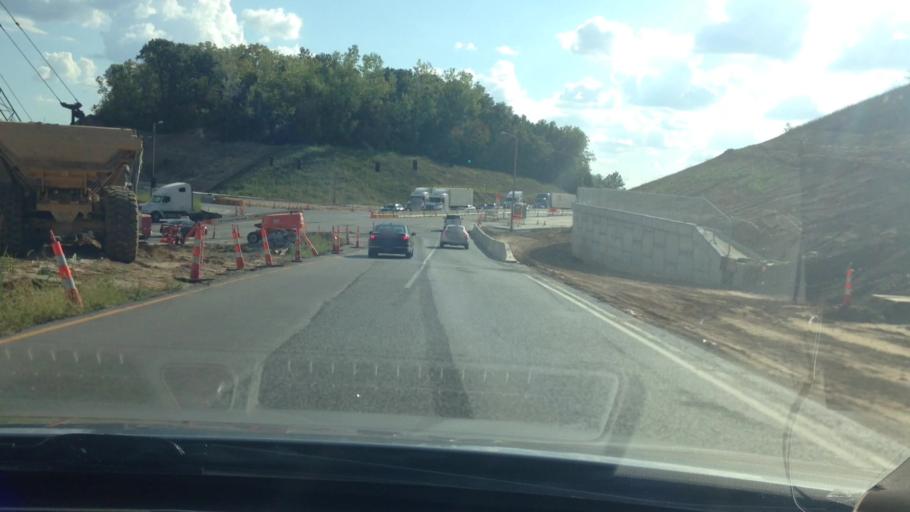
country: US
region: Missouri
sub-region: Clay County
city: Claycomo
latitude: 39.1596
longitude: -94.4978
